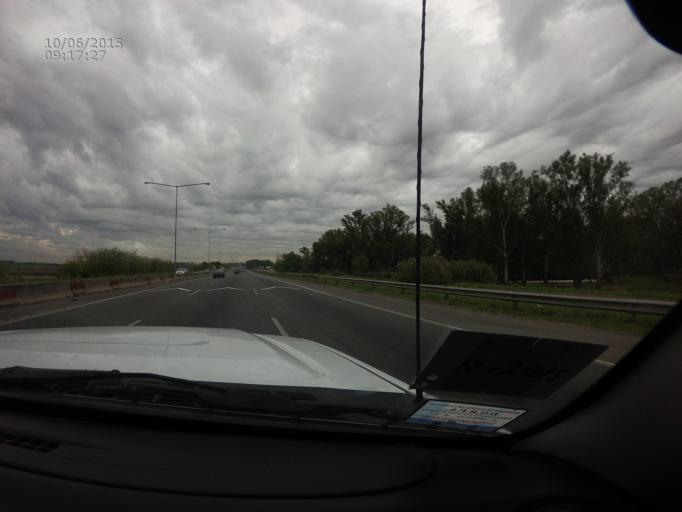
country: AR
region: Buenos Aires
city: Belen de Escobar
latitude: -34.2971
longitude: -58.8829
